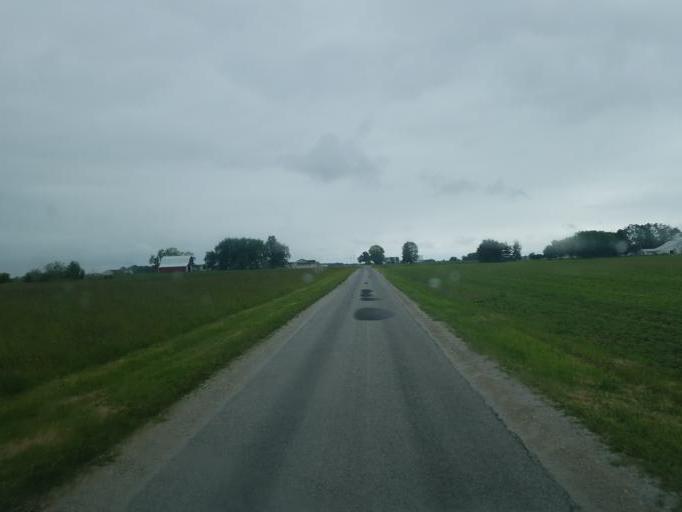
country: US
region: Ohio
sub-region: Marion County
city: Marion
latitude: 40.5607
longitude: -83.0147
